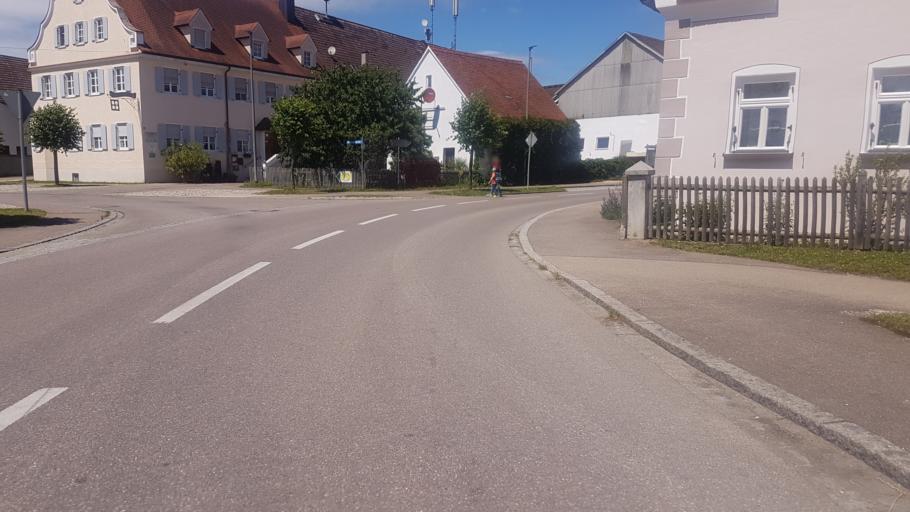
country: DE
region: Bavaria
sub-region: Swabia
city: Blindheim
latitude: 48.6318
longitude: 10.6185
